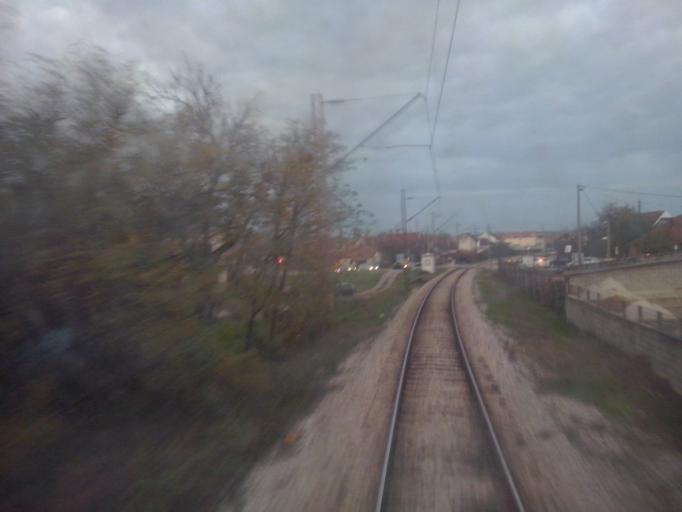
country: RS
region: Central Serbia
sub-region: Kolubarski Okrug
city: Valjevo
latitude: 44.2791
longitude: 19.9256
